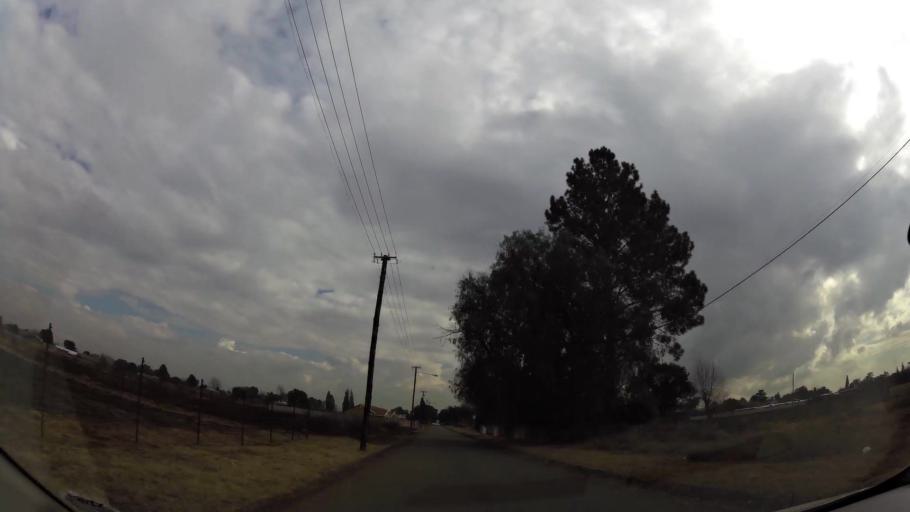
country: ZA
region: Gauteng
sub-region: Sedibeng District Municipality
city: Meyerton
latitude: -26.5960
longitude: 27.9972
